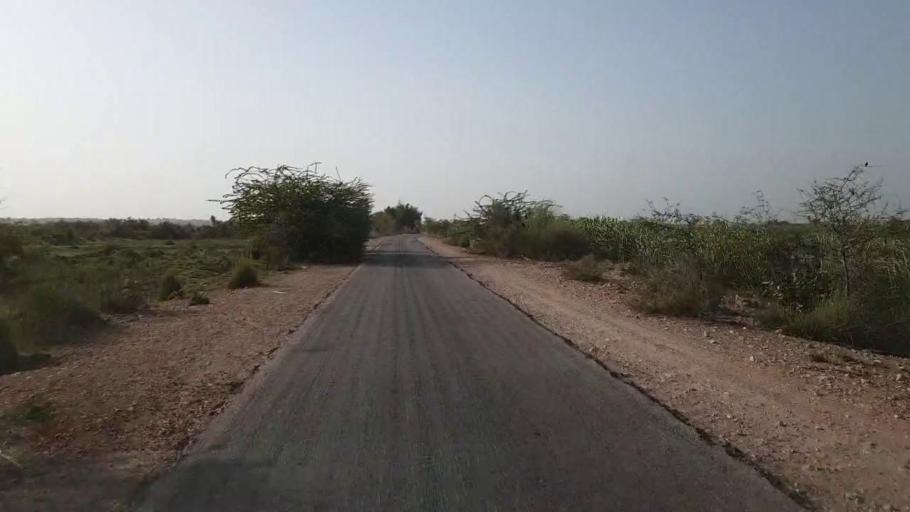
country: PK
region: Sindh
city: Jam Sahib
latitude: 26.4581
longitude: 68.8595
